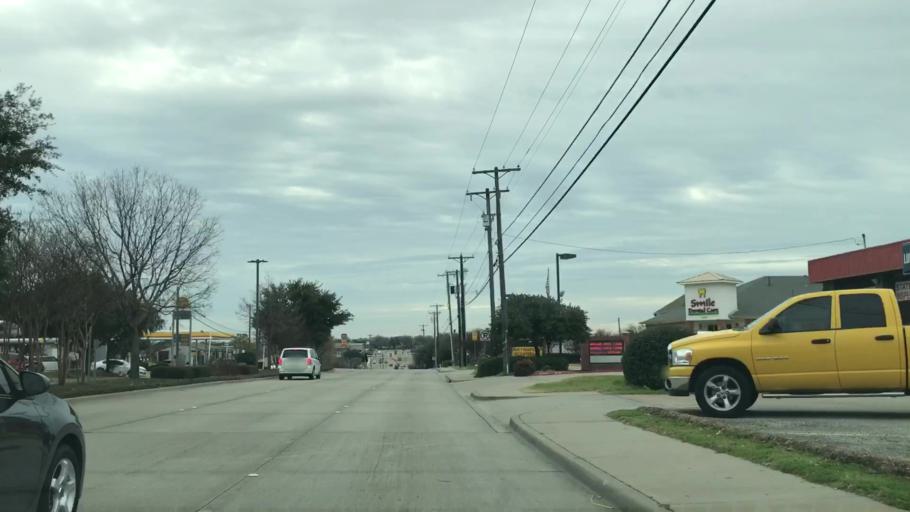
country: US
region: Texas
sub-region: Dallas County
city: Carrollton
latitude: 32.9427
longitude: -96.8906
